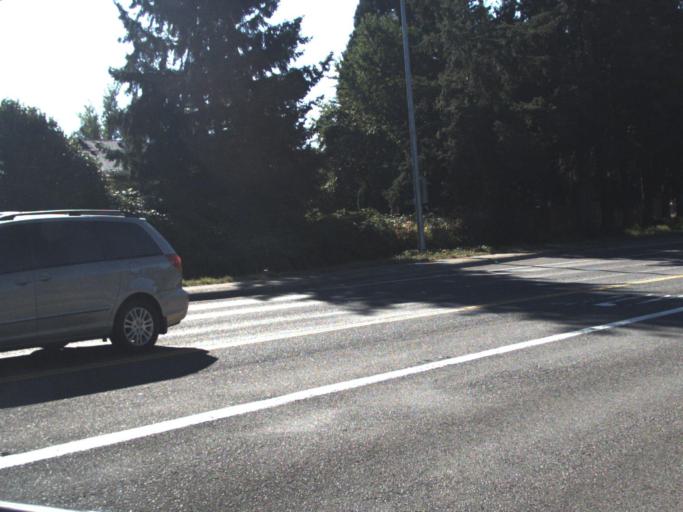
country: US
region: Washington
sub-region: King County
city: East Hill-Meridian
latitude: 47.4034
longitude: -122.1971
